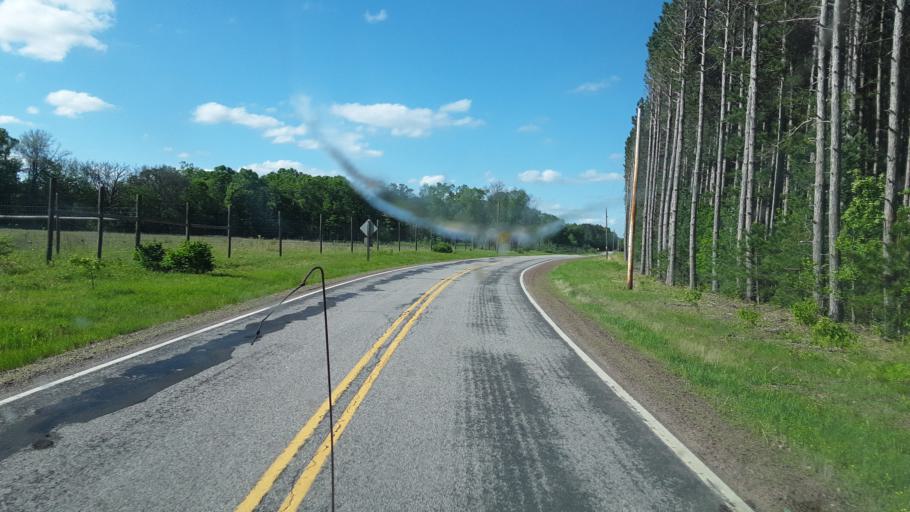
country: US
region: Wisconsin
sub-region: Wood County
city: Nekoosa
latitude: 44.3085
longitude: -90.1296
